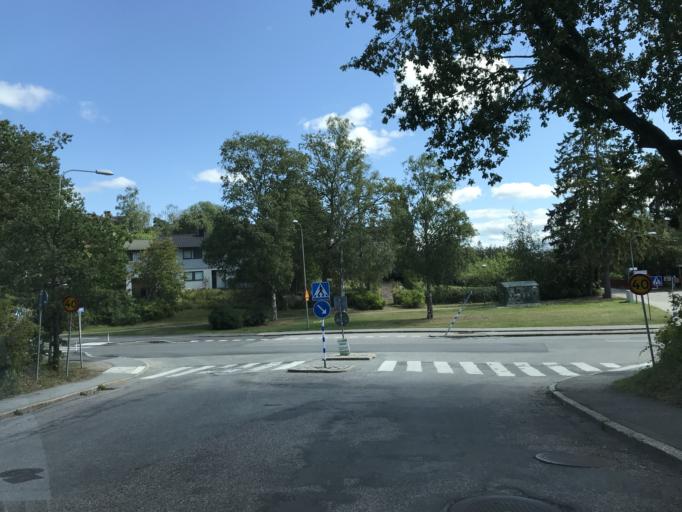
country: SE
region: Stockholm
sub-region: Huddinge Kommun
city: Segeltorp
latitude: 59.2947
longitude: 17.9539
